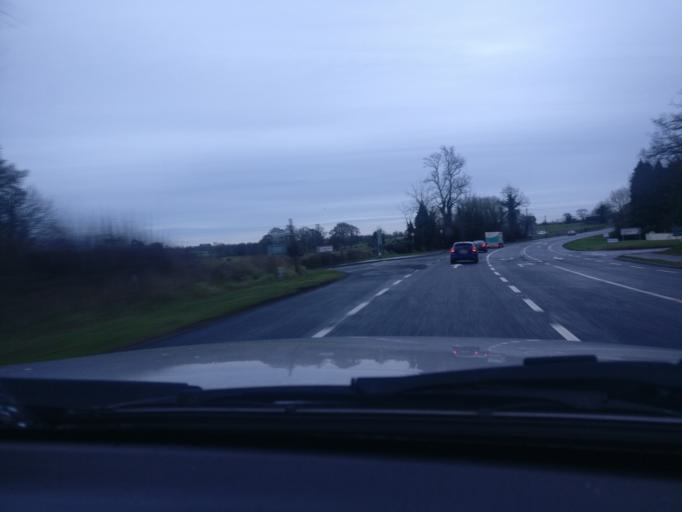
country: IE
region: Leinster
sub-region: An Mhi
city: Kells
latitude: 53.7082
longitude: -6.8007
